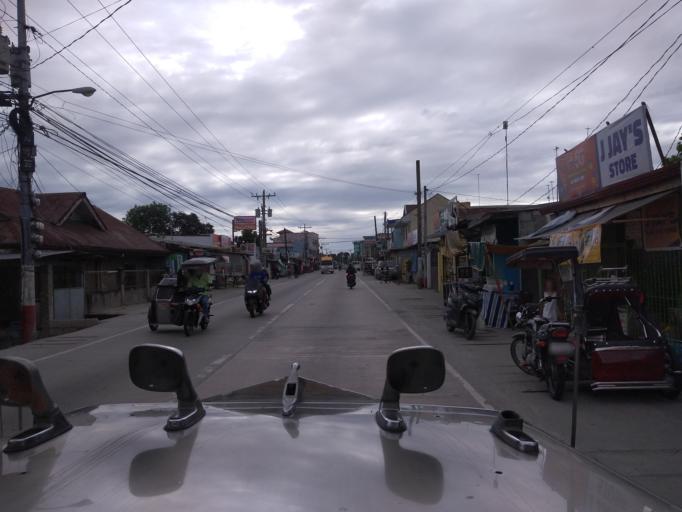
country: PH
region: Central Luzon
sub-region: Province of Pampanga
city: Pandacaqui
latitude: 15.1807
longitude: 120.6273
